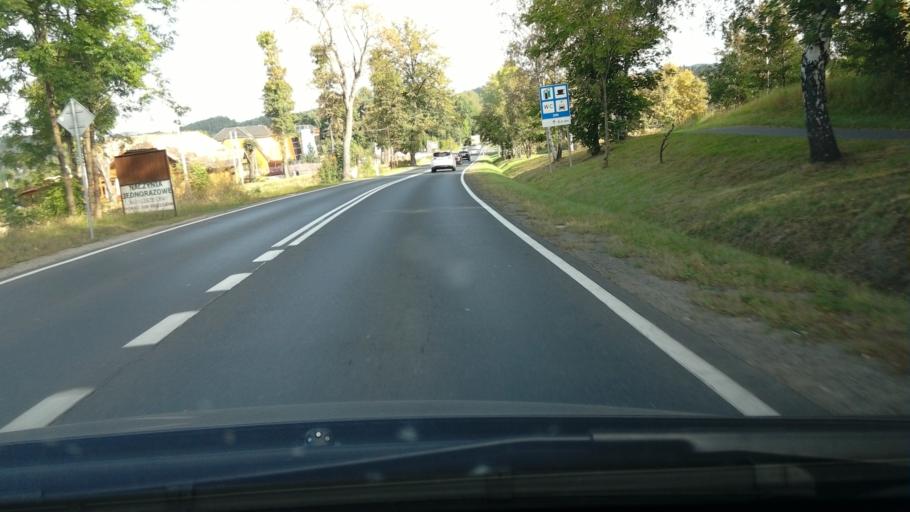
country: PL
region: Lower Silesian Voivodeship
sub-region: Jelenia Gora
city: Jelenia Gora
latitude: 50.8768
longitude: 15.7589
